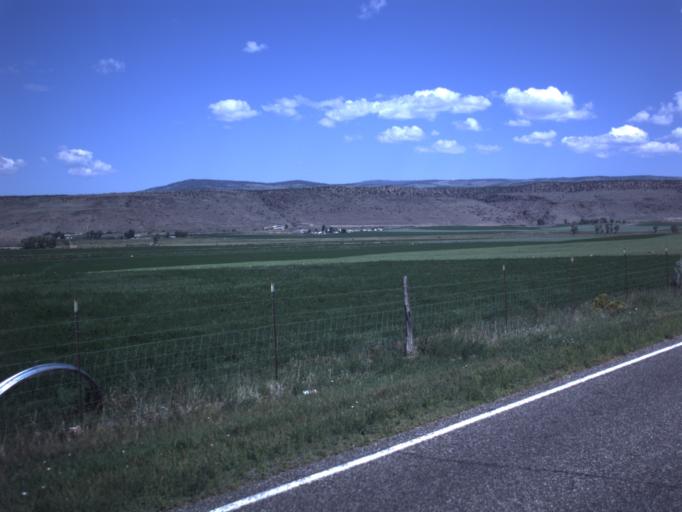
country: US
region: Utah
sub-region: Wayne County
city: Loa
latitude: 38.4269
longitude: -111.6202
